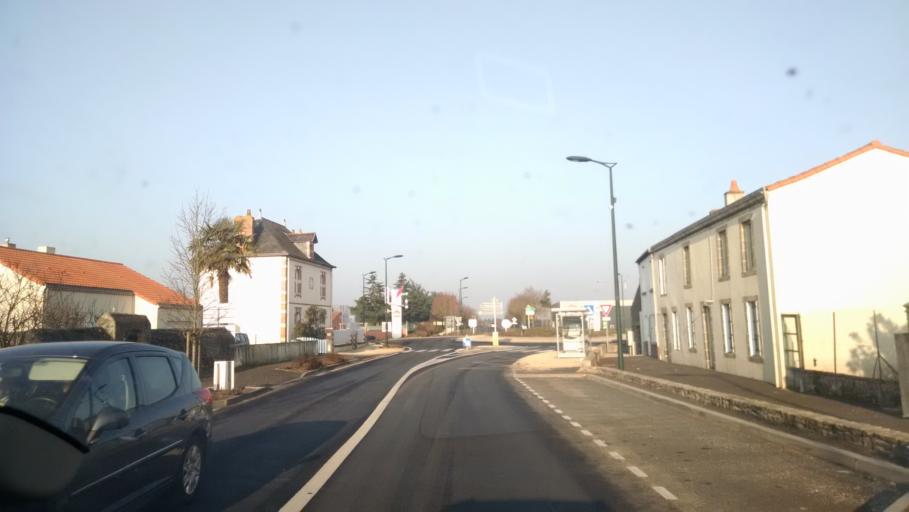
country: FR
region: Pays de la Loire
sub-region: Departement de la Loire-Atlantique
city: Remouille
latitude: 47.0579
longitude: -1.3743
